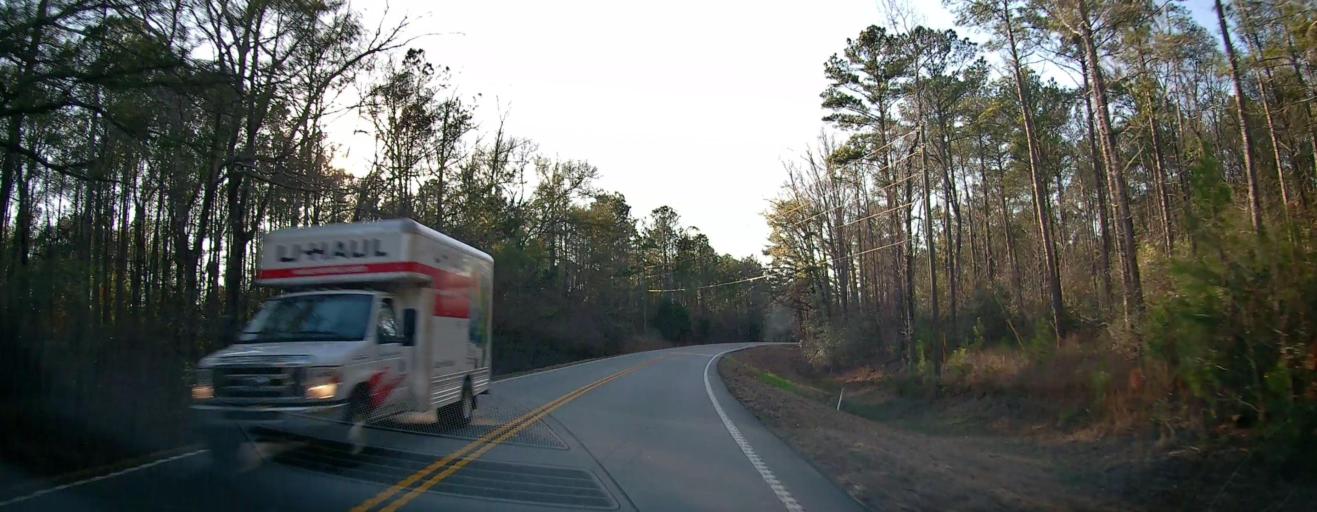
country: US
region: Alabama
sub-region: Chambers County
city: Valley
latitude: 32.7406
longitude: -85.0738
